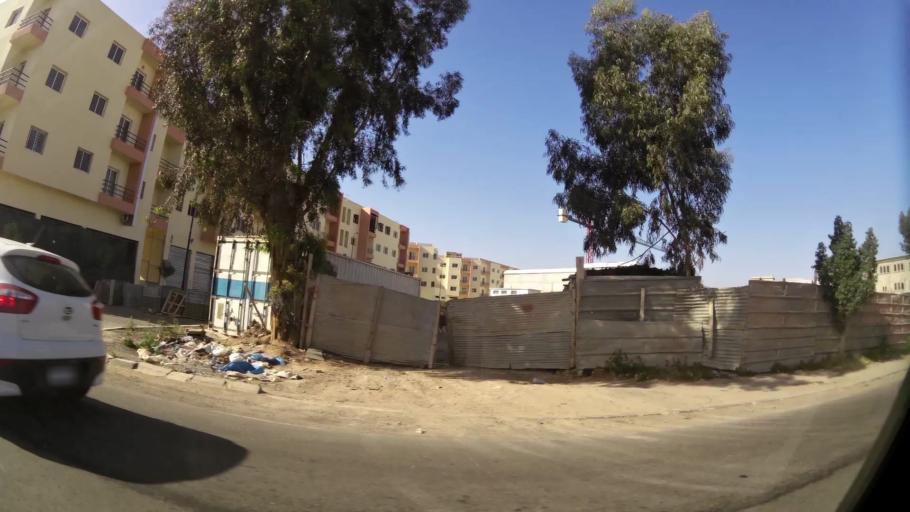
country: MA
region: Souss-Massa-Draa
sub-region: Inezgane-Ait Mellou
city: Inezgane
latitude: 30.3724
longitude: -9.5198
